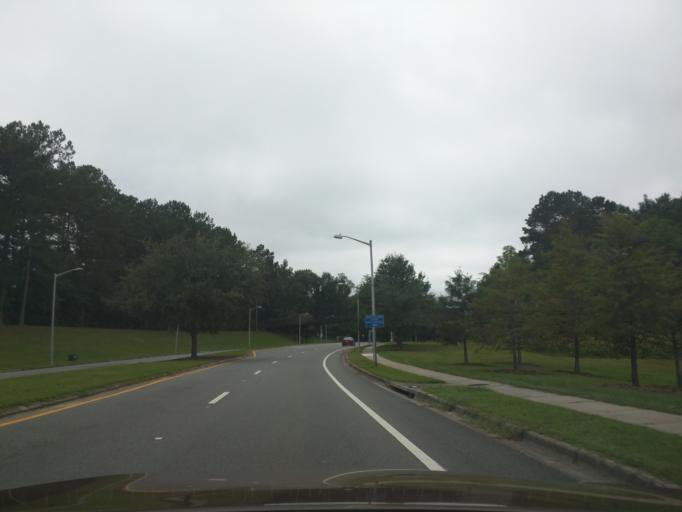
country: US
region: Florida
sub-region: Leon County
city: Tallahassee
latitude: 30.4405
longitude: -84.2080
